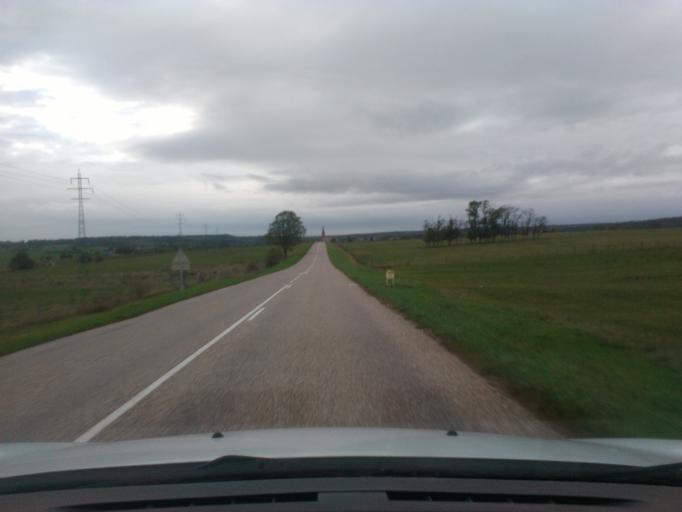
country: FR
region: Lorraine
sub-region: Departement des Vosges
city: Chatel-sur-Moselle
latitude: 48.3436
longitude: 6.4487
